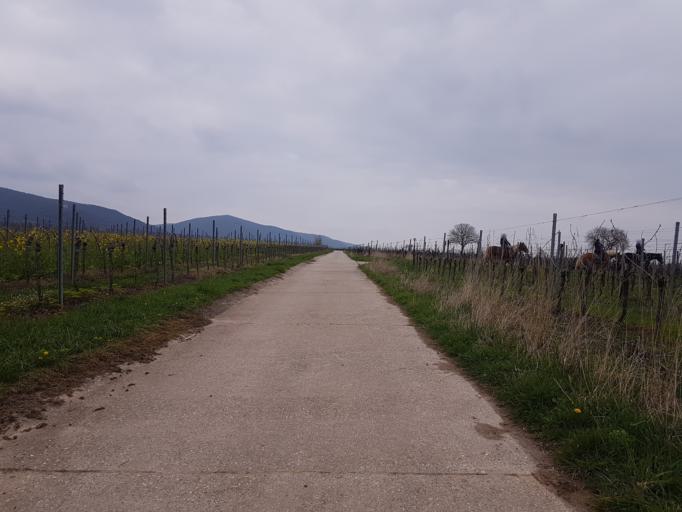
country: DE
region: Rheinland-Pfalz
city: Bochingen
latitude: 49.2307
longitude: 8.0797
